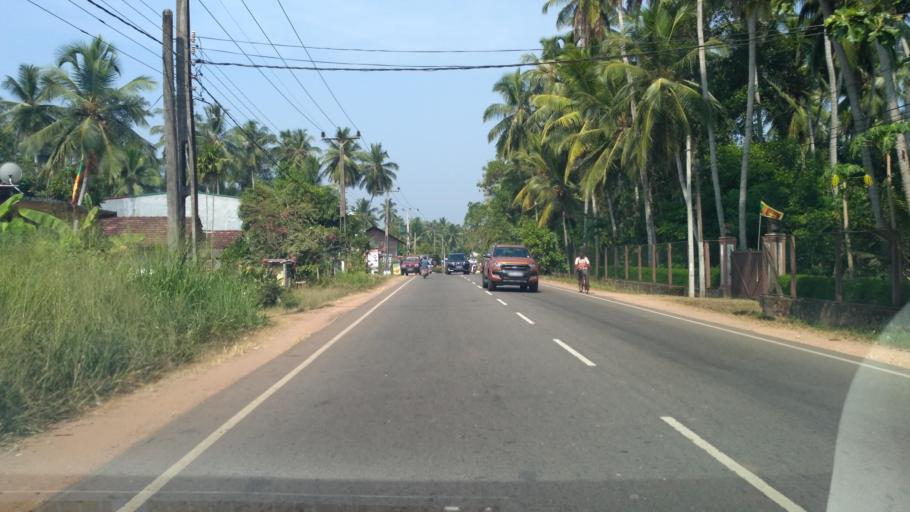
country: LK
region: North Western
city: Kuliyapitiya
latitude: 7.3319
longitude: 80.0138
